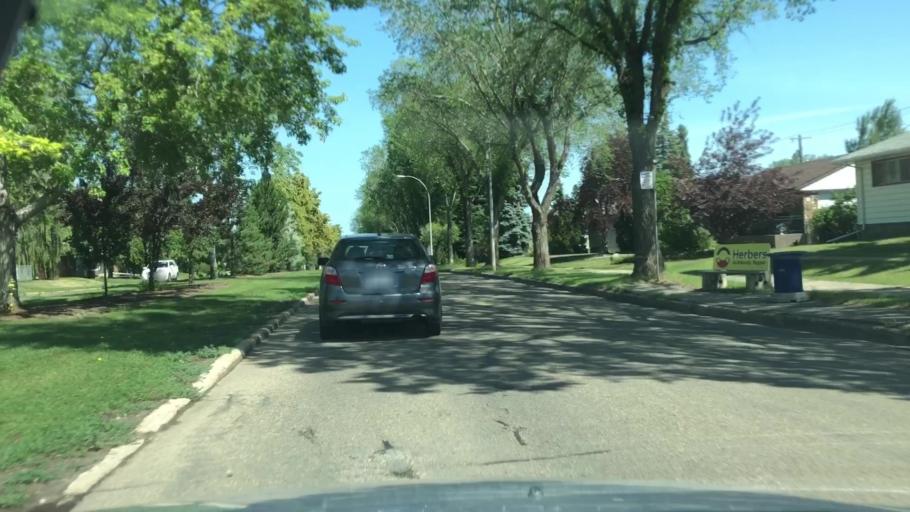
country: CA
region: Alberta
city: Edmonton
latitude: 53.5476
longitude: -113.4185
